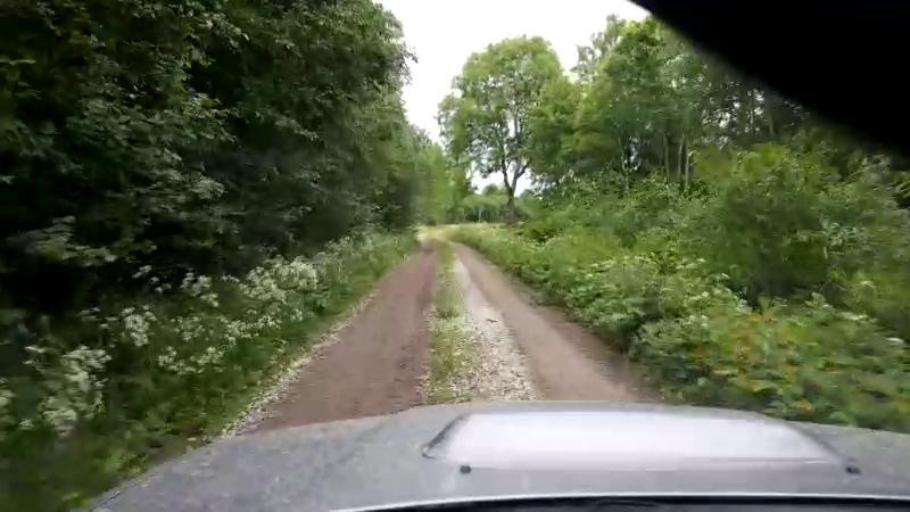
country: EE
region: Paernumaa
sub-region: Tootsi vald
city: Tootsi
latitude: 58.5932
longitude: 24.6632
